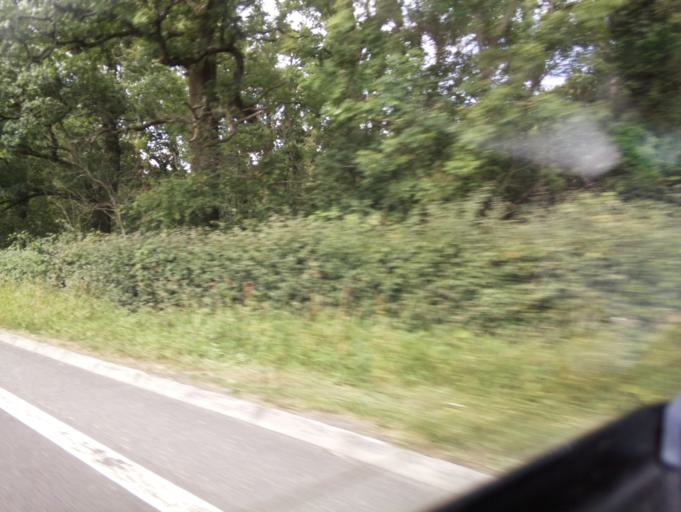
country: GB
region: England
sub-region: Somerset
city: Yeovil
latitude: 50.8663
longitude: -2.5953
